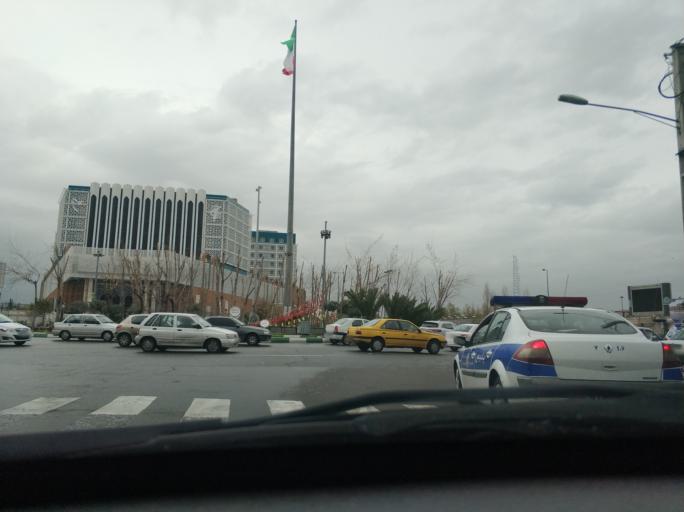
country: IR
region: Tehran
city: Tehran
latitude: 35.7061
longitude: 51.4402
